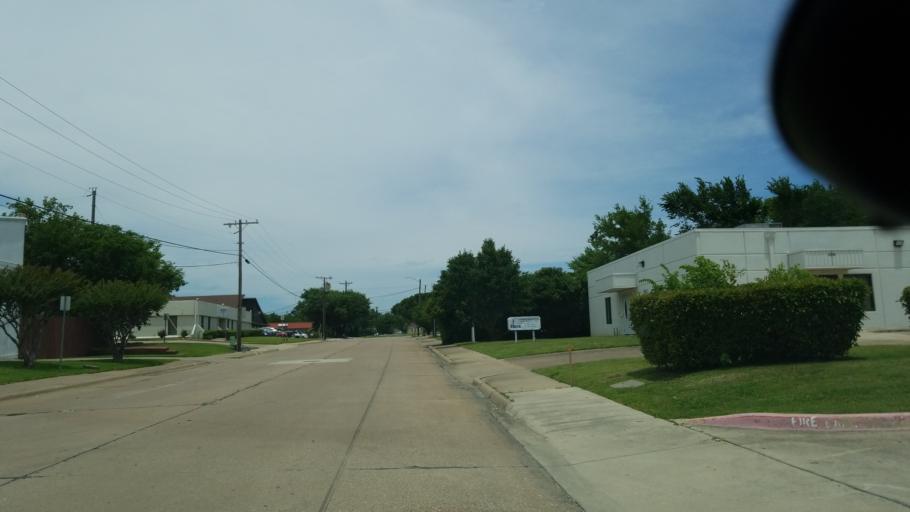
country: US
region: Texas
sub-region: Dallas County
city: Irving
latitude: 32.8407
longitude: -96.9728
